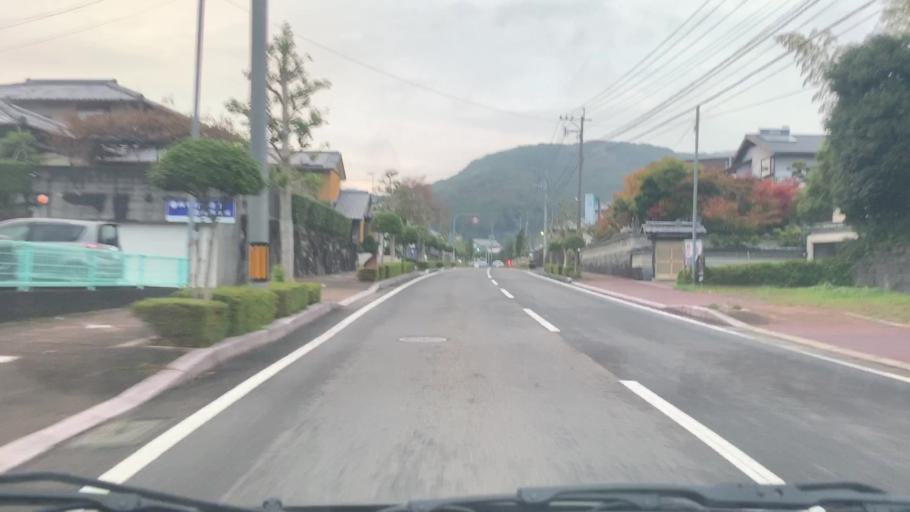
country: JP
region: Saga Prefecture
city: Ureshinomachi-shimojuku
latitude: 33.1477
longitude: 129.9002
